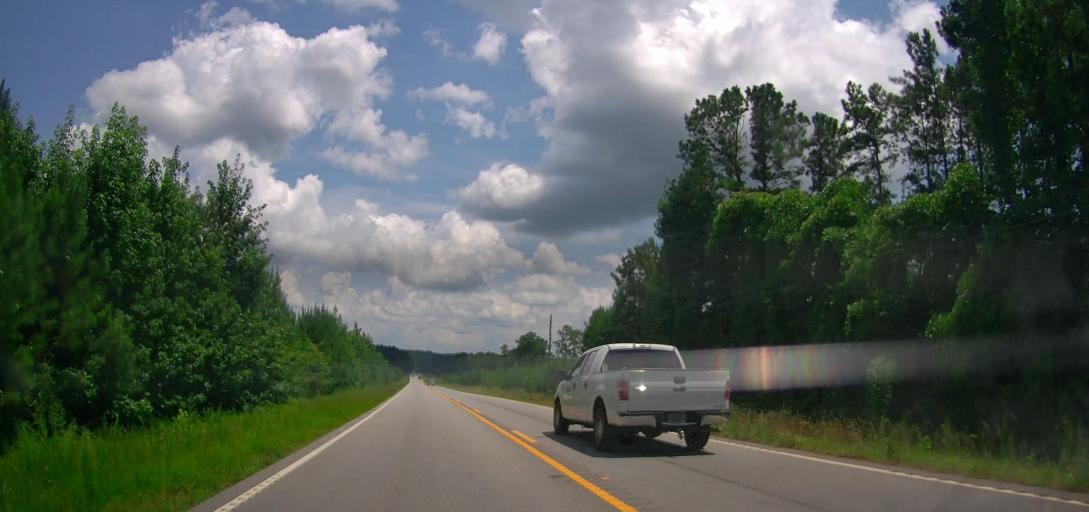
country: US
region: Georgia
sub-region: Meriwether County
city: Greenville
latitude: 33.0232
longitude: -84.6850
